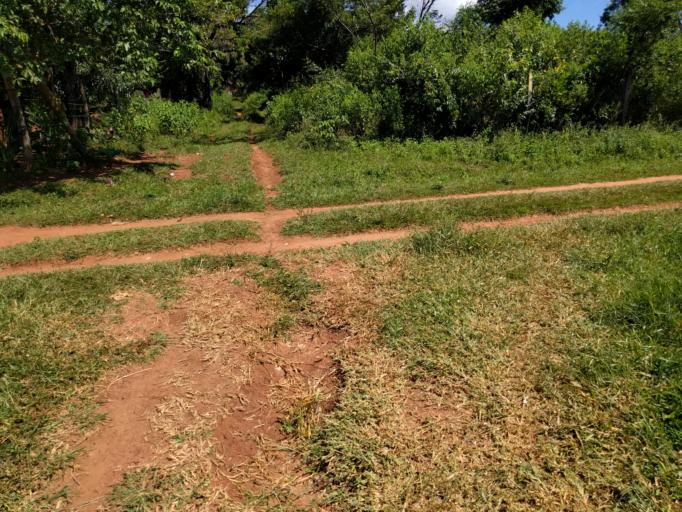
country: BO
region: Santa Cruz
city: Robore
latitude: -18.3372
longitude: -59.5976
